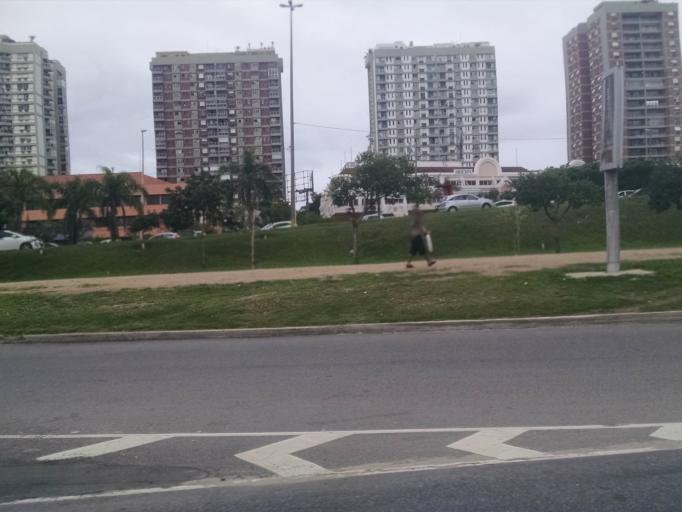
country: BR
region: Rio de Janeiro
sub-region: Rio De Janeiro
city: Rio de Janeiro
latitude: -22.9995
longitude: -43.3621
